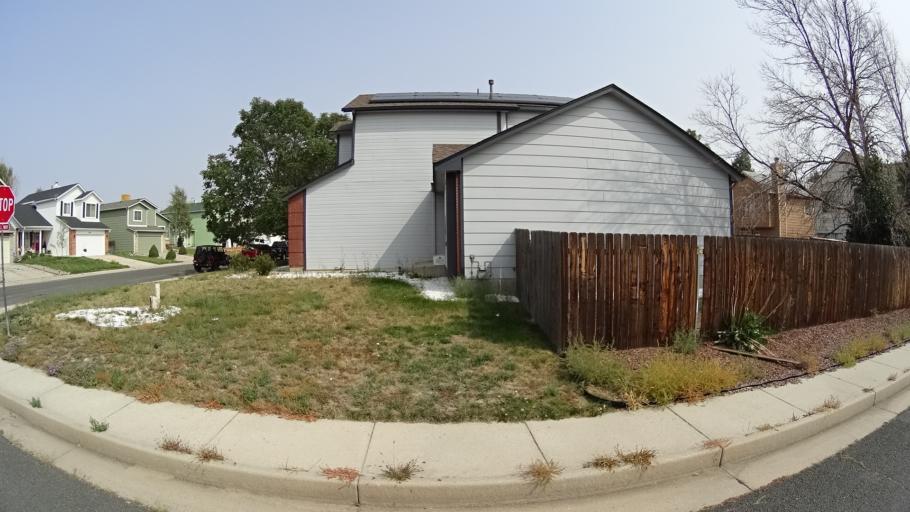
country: US
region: Colorado
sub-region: El Paso County
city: Cimarron Hills
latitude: 38.9217
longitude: -104.7244
